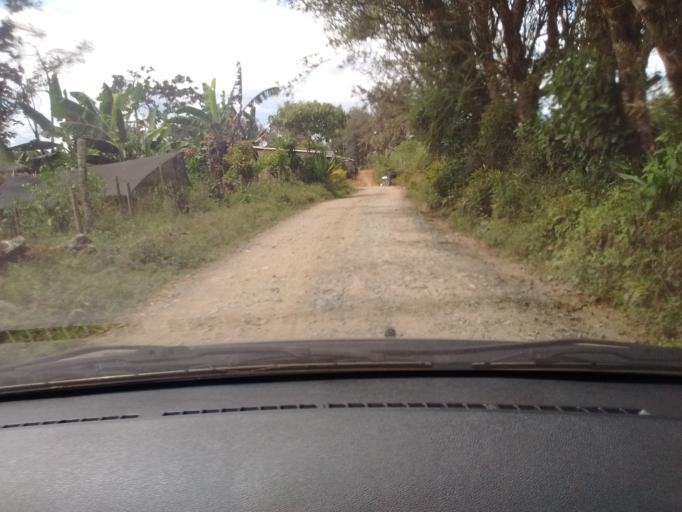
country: CO
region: Cauca
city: El Tambo
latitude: 2.4576
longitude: -76.8206
